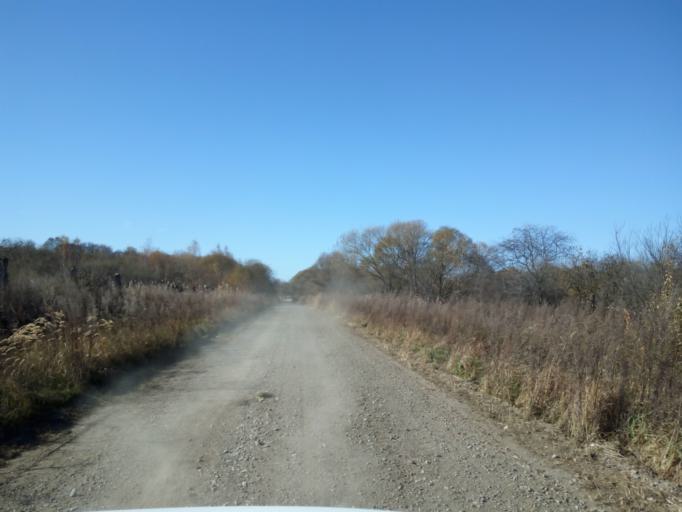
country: RU
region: Primorskiy
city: Dal'nerechensk
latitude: 45.9406
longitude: 133.6789
